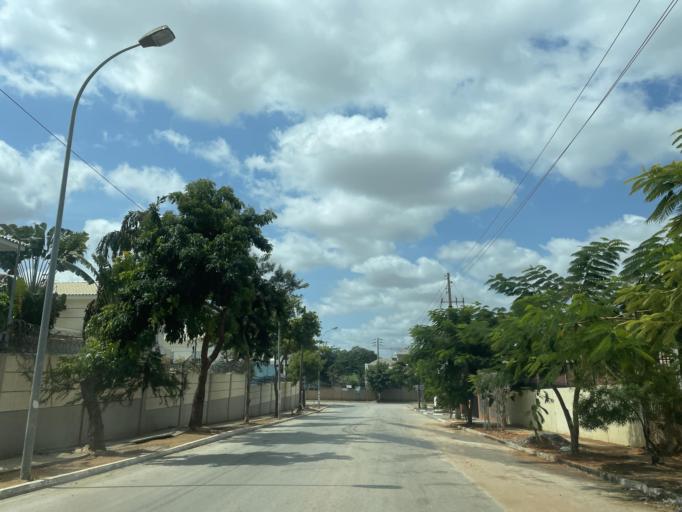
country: AO
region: Luanda
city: Luanda
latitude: -8.9304
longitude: 13.1834
